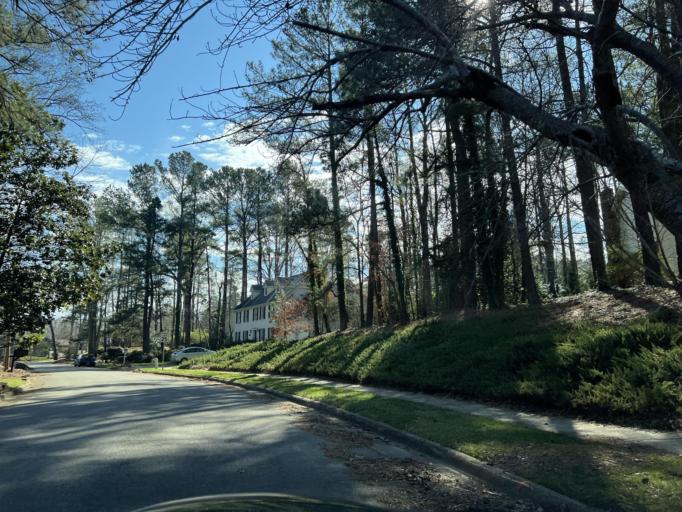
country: US
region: North Carolina
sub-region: Wake County
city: West Raleigh
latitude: 35.8844
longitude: -78.6208
